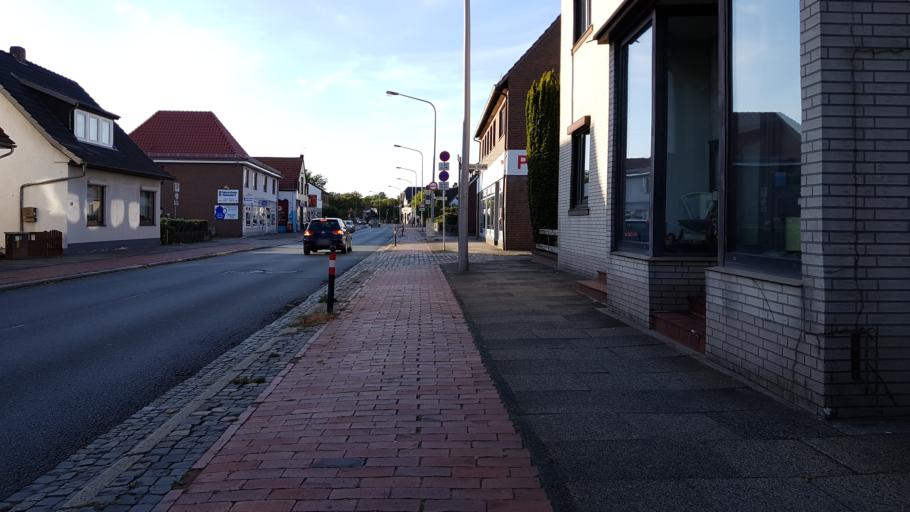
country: DE
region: Lower Saxony
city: Riede
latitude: 53.0368
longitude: 8.9472
